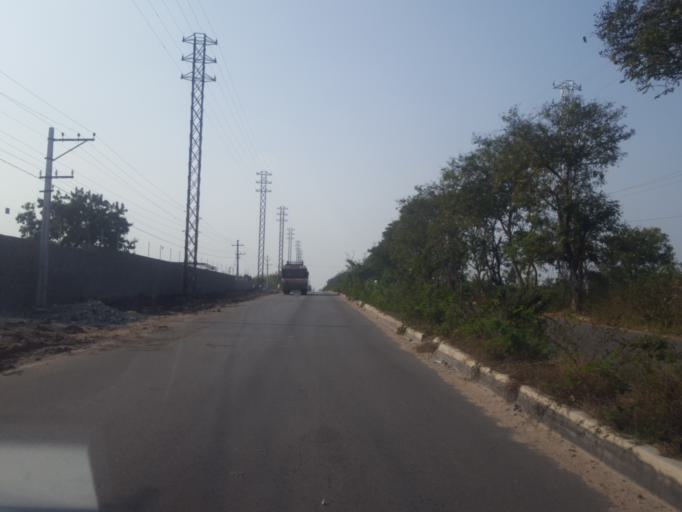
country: IN
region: Telangana
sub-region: Medak
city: Serilingampalle
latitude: 17.4080
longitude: 78.2779
